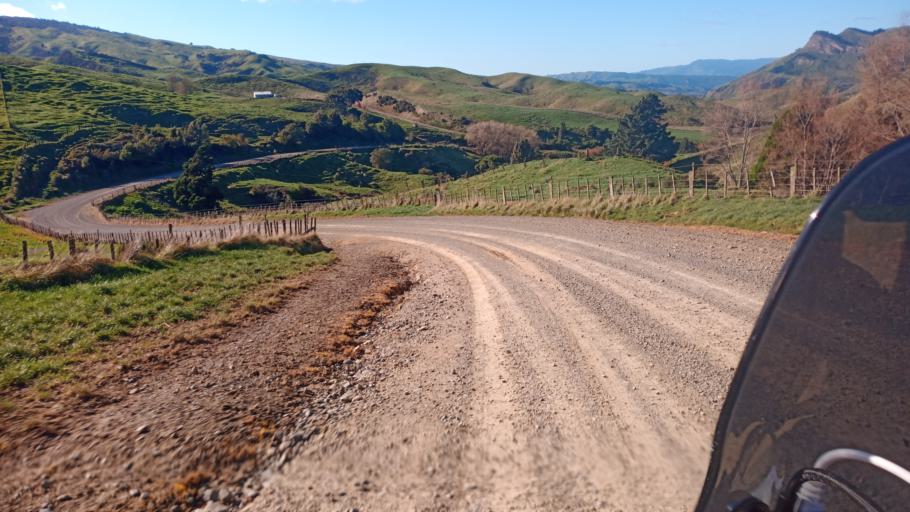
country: NZ
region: Hawke's Bay
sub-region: Wairoa District
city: Wairoa
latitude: -38.7399
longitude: 177.2861
